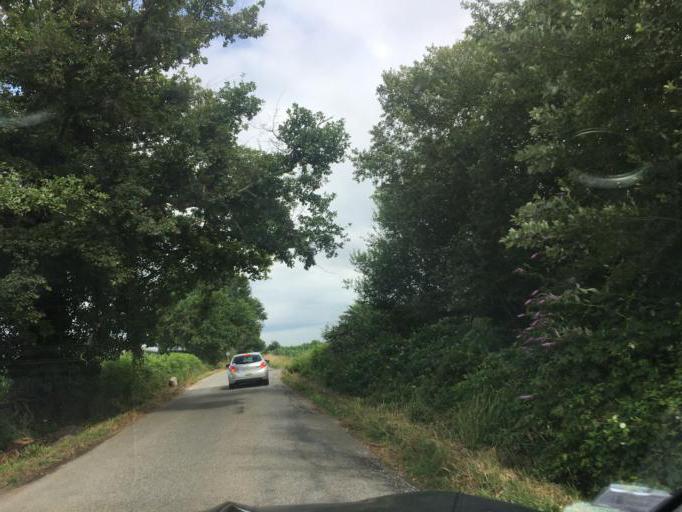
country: FR
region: Aquitaine
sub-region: Departement des Pyrenees-Atlantiques
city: Buros
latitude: 43.3162
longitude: -0.2961
